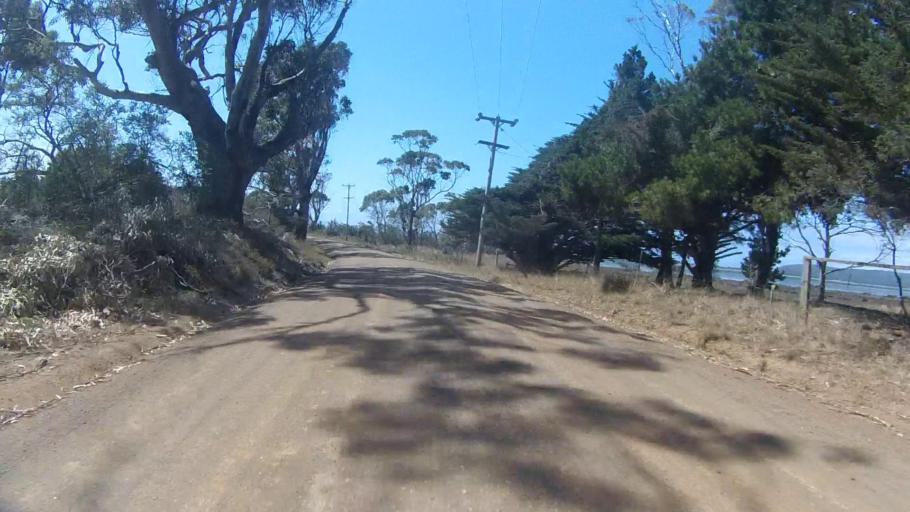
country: AU
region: Tasmania
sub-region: Sorell
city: Sorell
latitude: -42.8431
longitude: 147.8515
